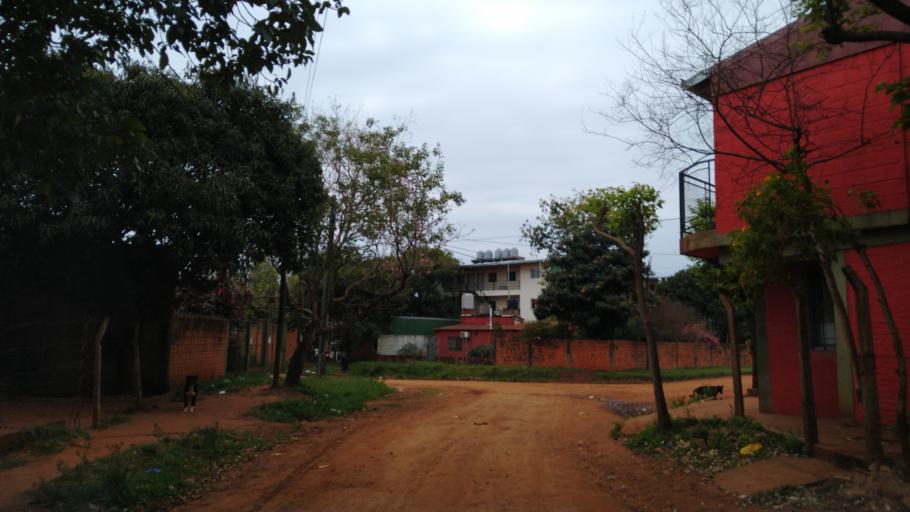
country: AR
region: Misiones
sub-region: Departamento de Capital
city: Posadas
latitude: -27.4369
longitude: -55.8854
